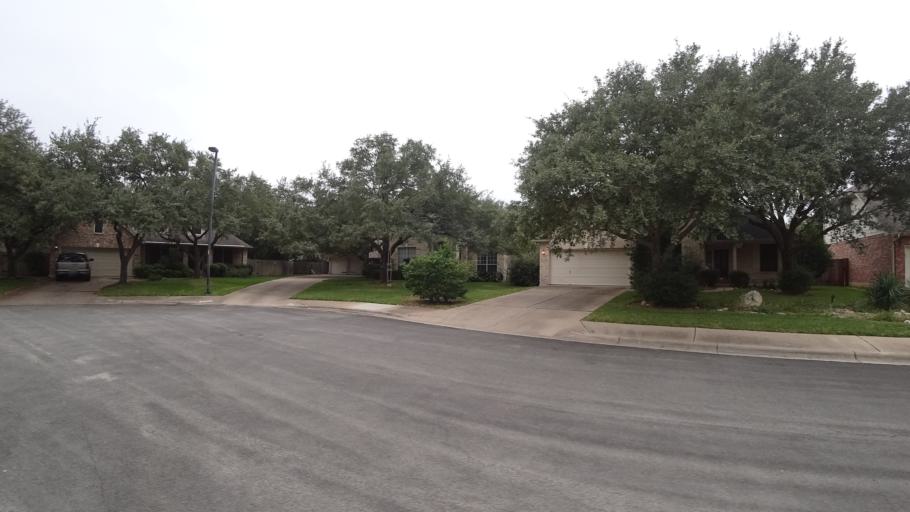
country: US
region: Texas
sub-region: Travis County
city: Shady Hollow
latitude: 30.1864
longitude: -97.8857
